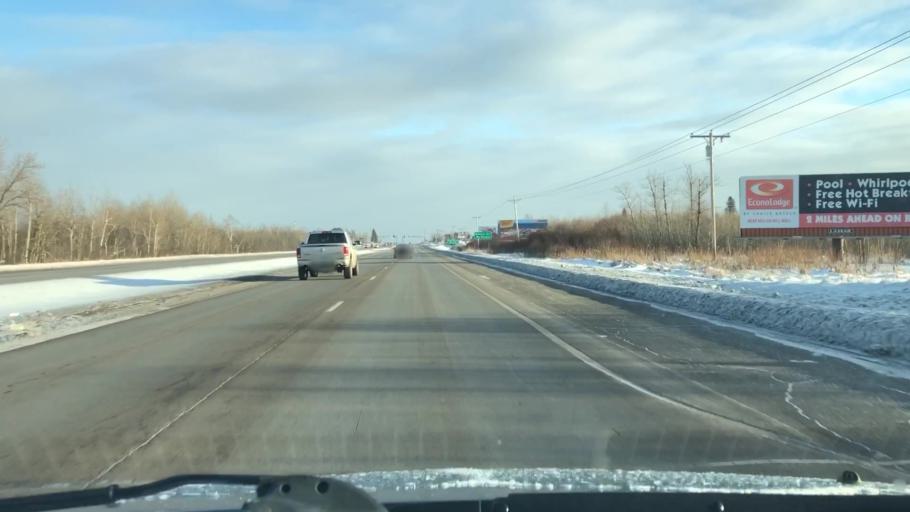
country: US
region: Minnesota
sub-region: Saint Louis County
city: Hermantown
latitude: 46.8313
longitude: -92.2018
